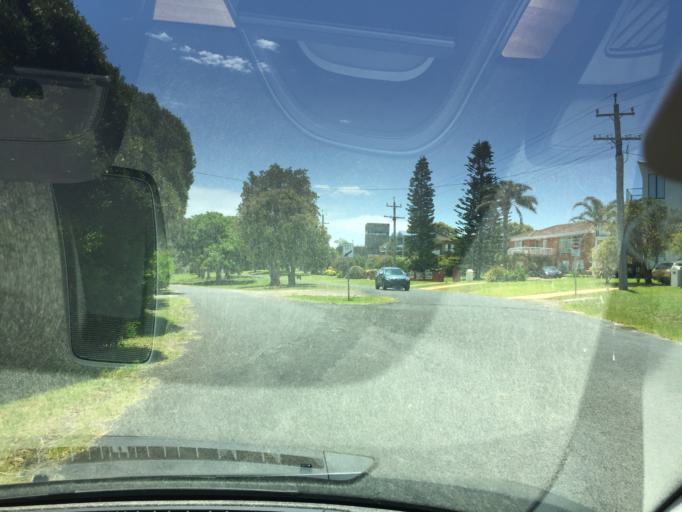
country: AU
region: New South Wales
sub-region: Bega Valley
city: Merimbula
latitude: -36.8955
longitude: 149.9268
